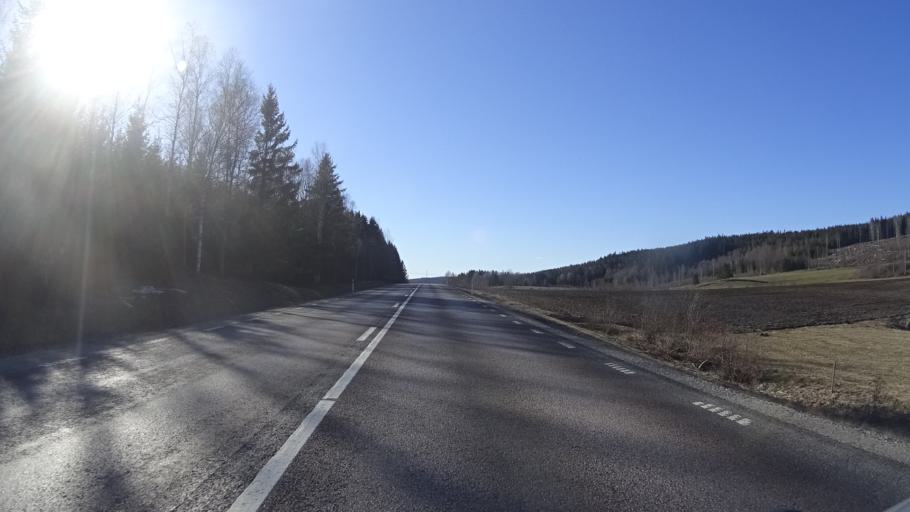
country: SE
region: Vaermland
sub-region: Arvika Kommun
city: Arvika
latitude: 59.6681
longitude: 12.8276
